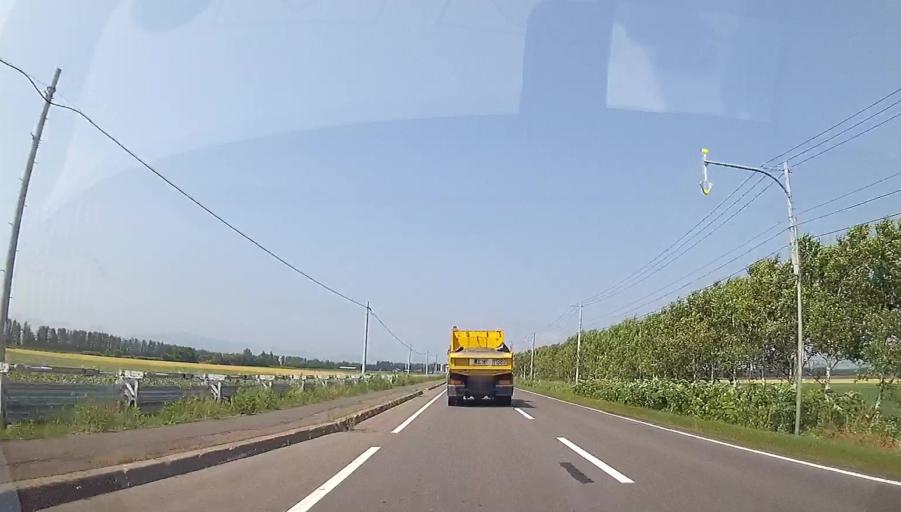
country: JP
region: Hokkaido
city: Otofuke
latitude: 43.1113
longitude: 143.2329
